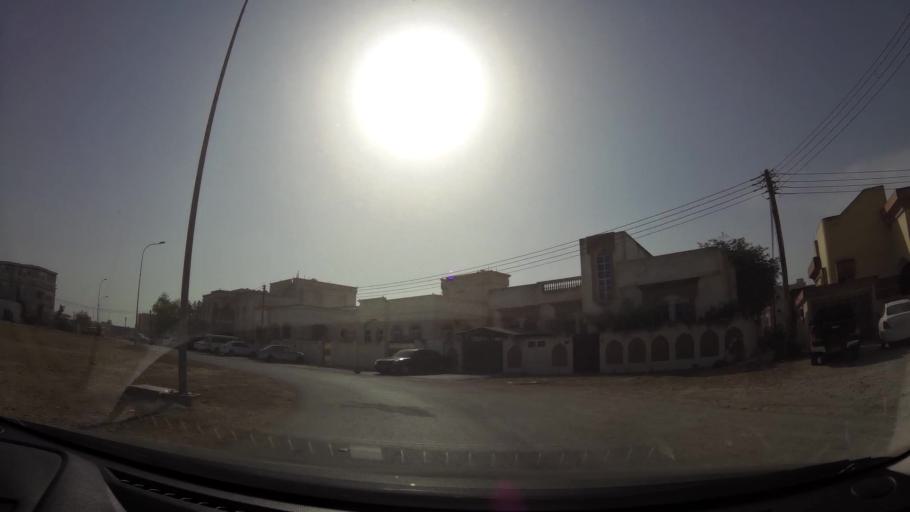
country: OM
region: Zufar
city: Salalah
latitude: 17.0091
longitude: 54.0162
